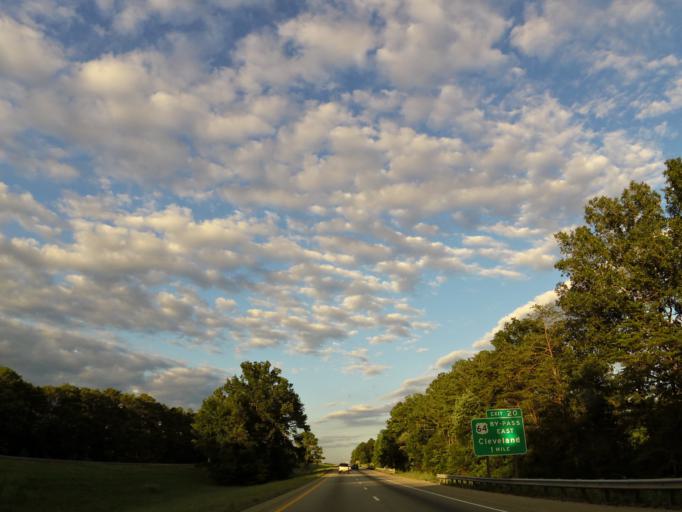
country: US
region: Tennessee
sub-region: Bradley County
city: Cleveland
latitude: 35.1464
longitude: -84.9664
